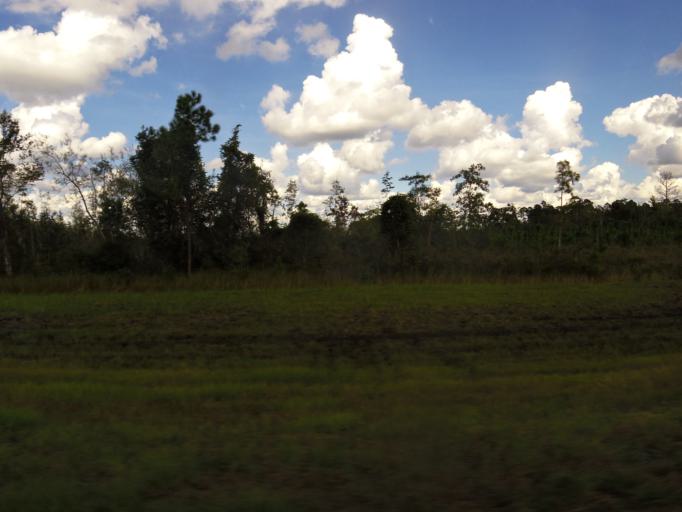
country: US
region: Georgia
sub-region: Echols County
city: Statenville
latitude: 30.6877
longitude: -82.8907
